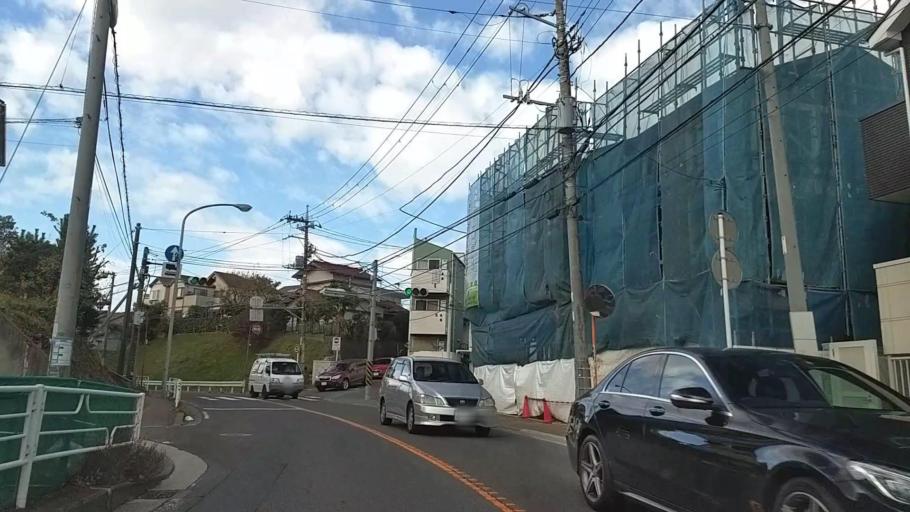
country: JP
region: Kanagawa
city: Yokohama
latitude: 35.5100
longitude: 139.6378
